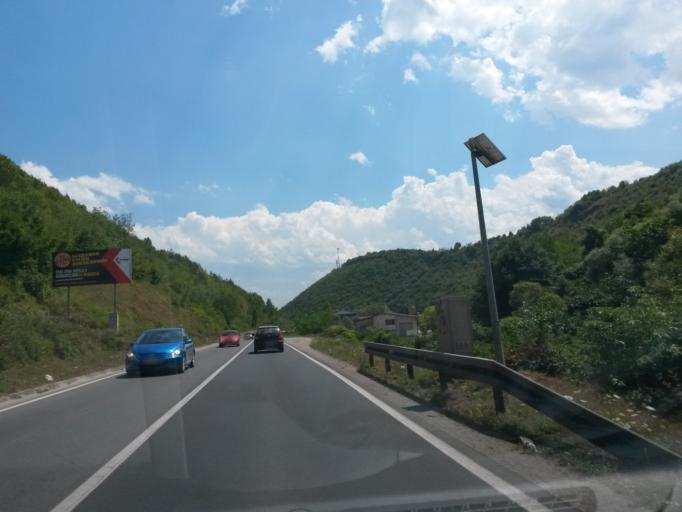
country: BA
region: Federation of Bosnia and Herzegovina
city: Travnik
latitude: 44.2266
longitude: 17.6820
